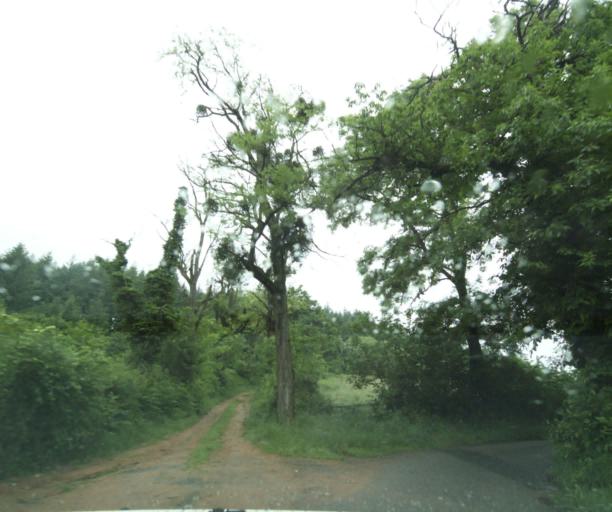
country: FR
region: Bourgogne
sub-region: Departement de Saone-et-Loire
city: La Clayette
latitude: 46.3536
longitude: 4.3617
